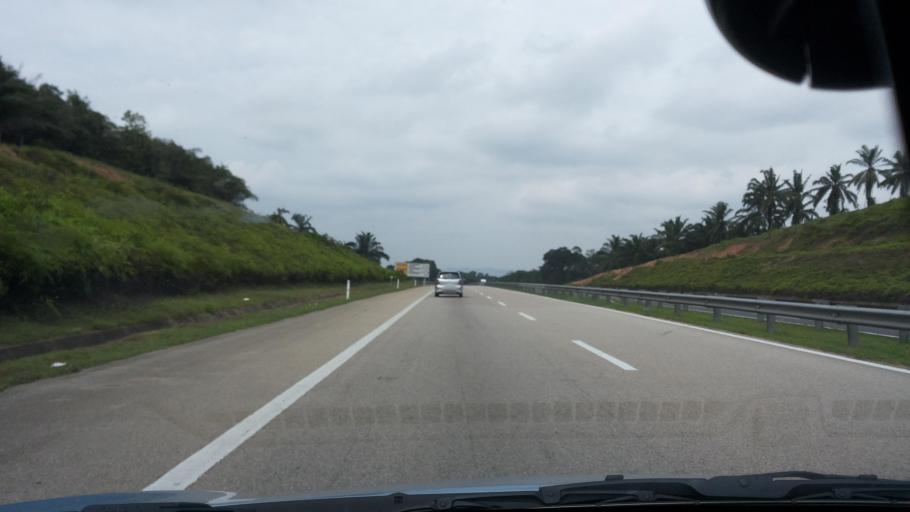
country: MY
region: Pahang
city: Kuantan
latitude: 3.8381
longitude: 103.1924
